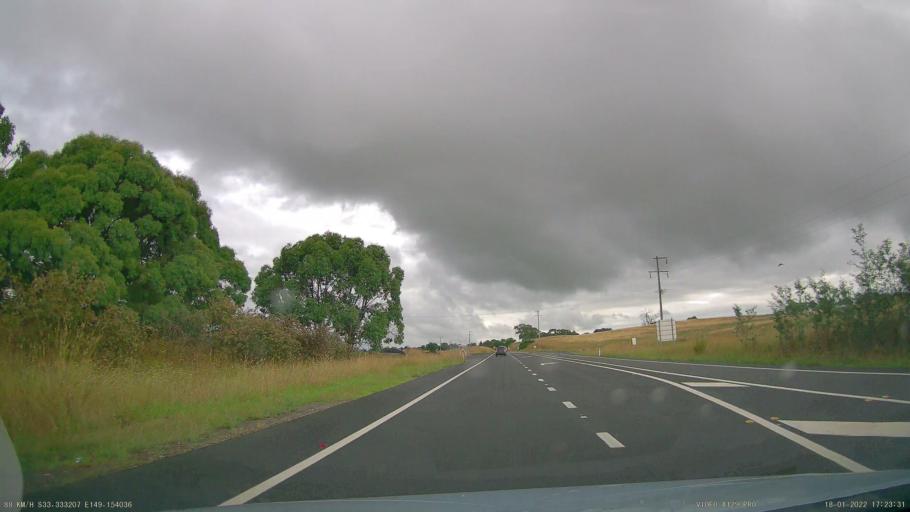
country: AU
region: New South Wales
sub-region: Orange Municipality
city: Orange
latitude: -33.3335
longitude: 149.1541
